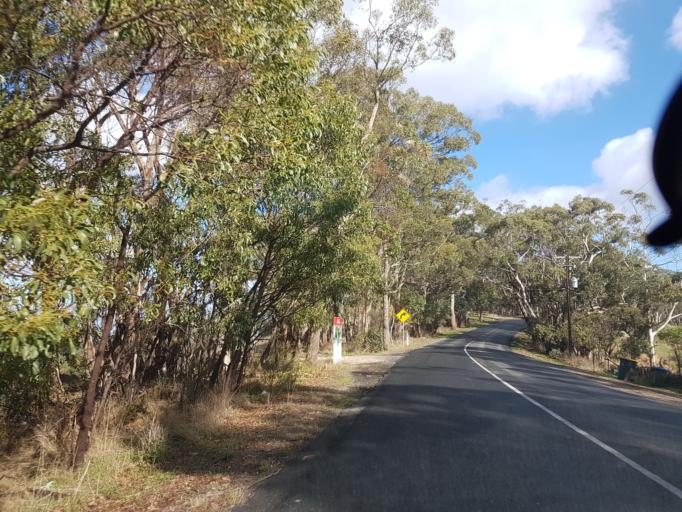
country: AU
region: South Australia
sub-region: Adelaide Hills
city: Heathfield
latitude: -35.0452
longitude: 138.7008
